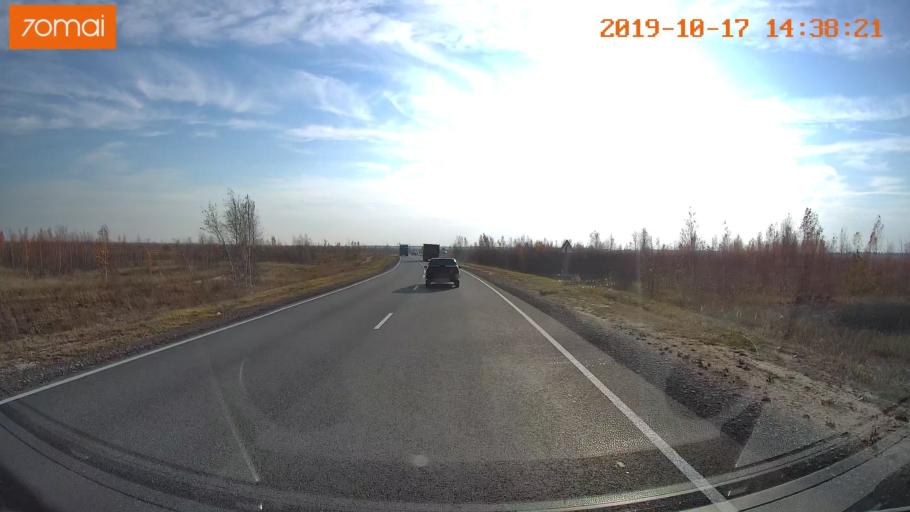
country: RU
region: Rjazan
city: Solotcha
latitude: 54.8713
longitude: 39.9850
